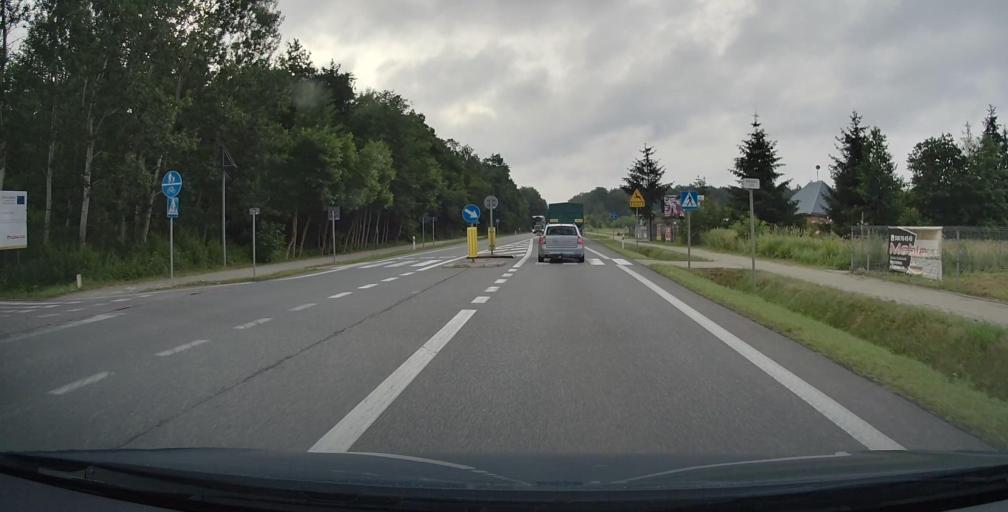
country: PL
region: Masovian Voivodeship
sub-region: Powiat siedlecki
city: Zbuczyn
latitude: 52.0849
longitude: 22.4573
